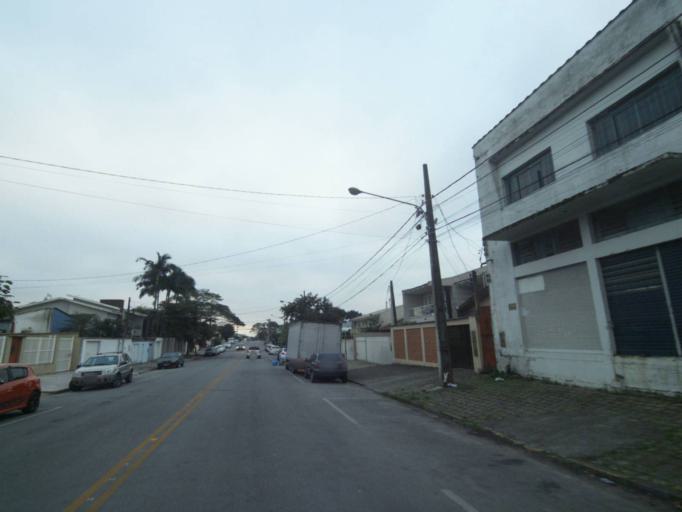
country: BR
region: Parana
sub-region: Paranagua
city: Paranagua
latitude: -25.5170
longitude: -48.5160
